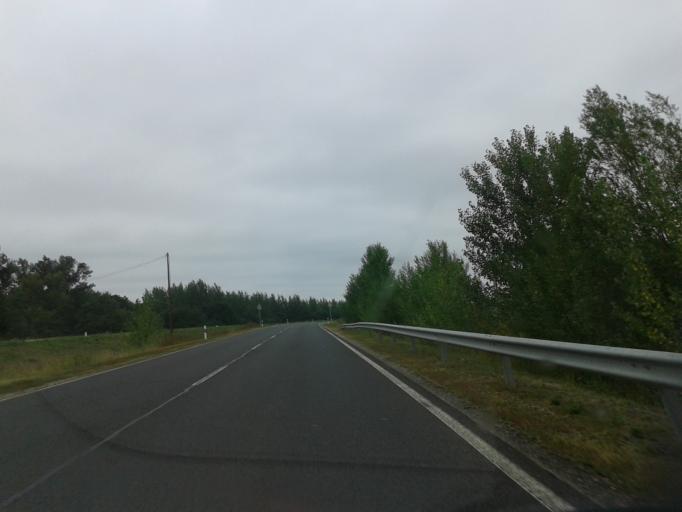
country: HU
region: Bacs-Kiskun
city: Harta
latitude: 46.7222
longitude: 19.0196
